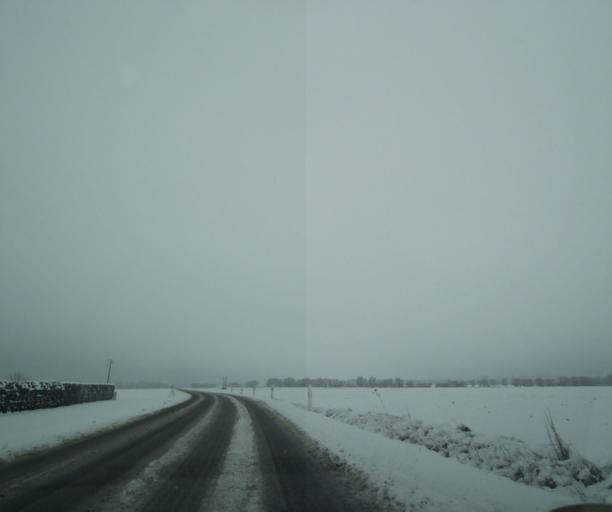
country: FR
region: Champagne-Ardenne
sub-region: Departement de la Haute-Marne
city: Saint-Dizier
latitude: 48.5783
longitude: 4.9065
